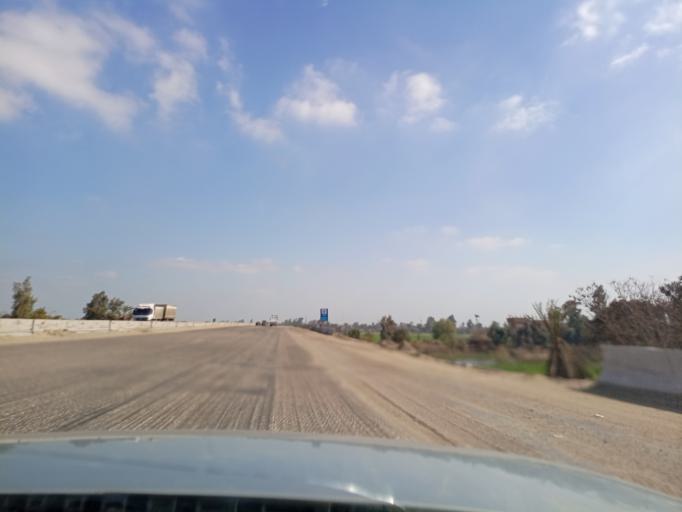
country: EG
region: Muhafazat al Minufiyah
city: Al Bajur
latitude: 30.4189
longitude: 31.0782
